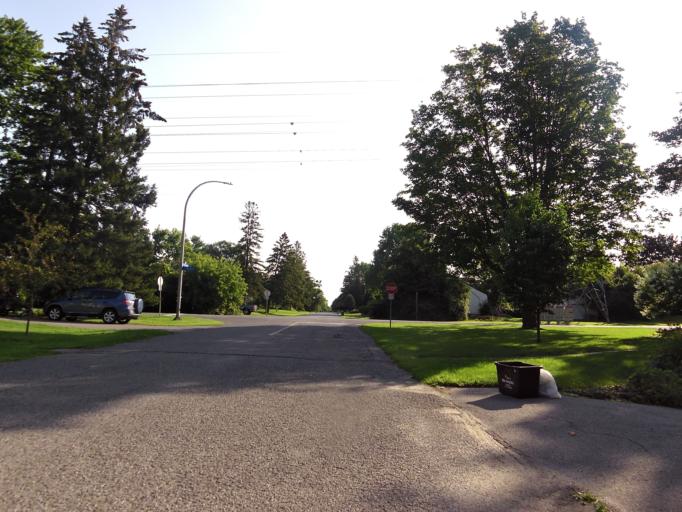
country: CA
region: Ontario
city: Ottawa
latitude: 45.3542
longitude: -75.7447
